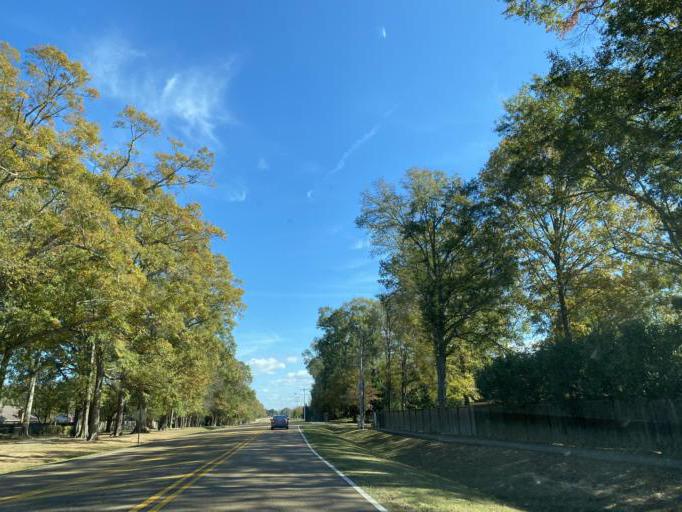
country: US
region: Mississippi
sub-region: Madison County
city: Madison
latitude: 32.4575
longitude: -90.1003
